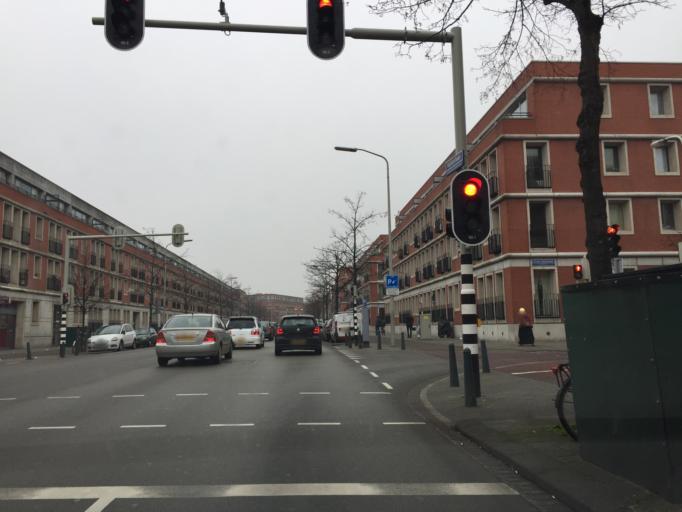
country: NL
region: South Holland
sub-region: Gemeente Den Haag
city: The Hague
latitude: 52.0644
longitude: 4.3096
